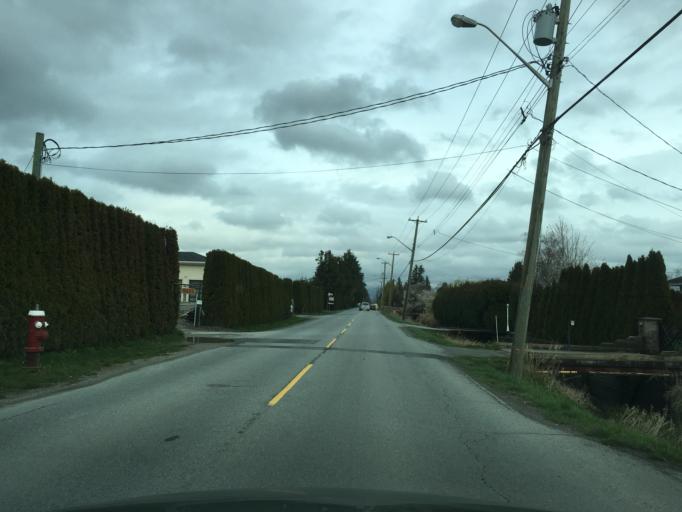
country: CA
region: British Columbia
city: Ladner
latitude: 49.1434
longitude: -123.0694
